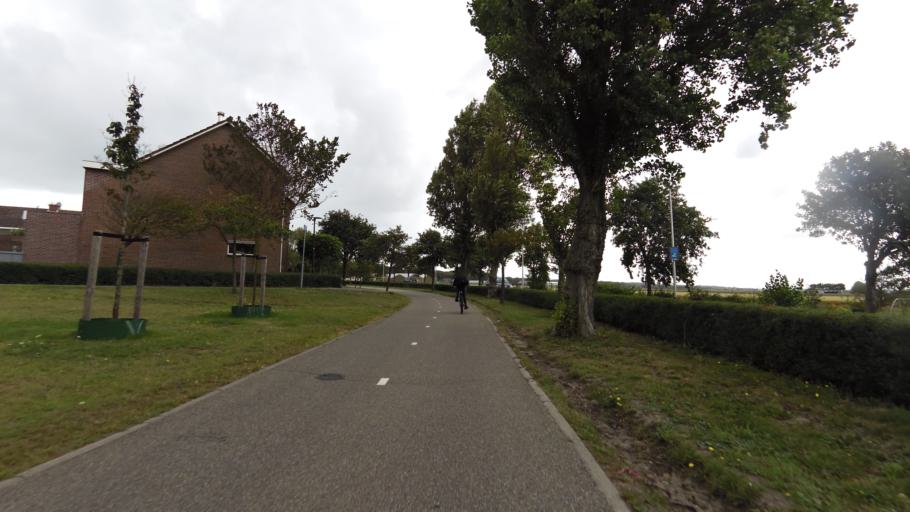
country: NL
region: South Holland
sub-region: Gemeente Noordwijk
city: Noordwijk-Binnen
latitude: 52.2465
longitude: 4.4527
